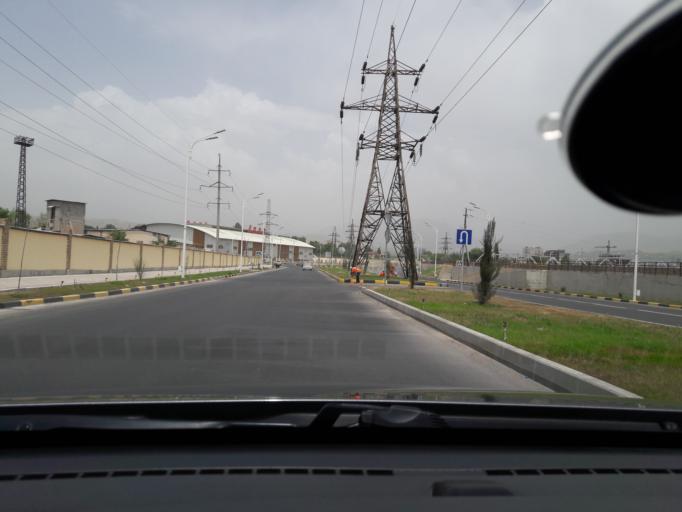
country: TJ
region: Dushanbe
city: Dushanbe
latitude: 38.5649
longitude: 68.7684
